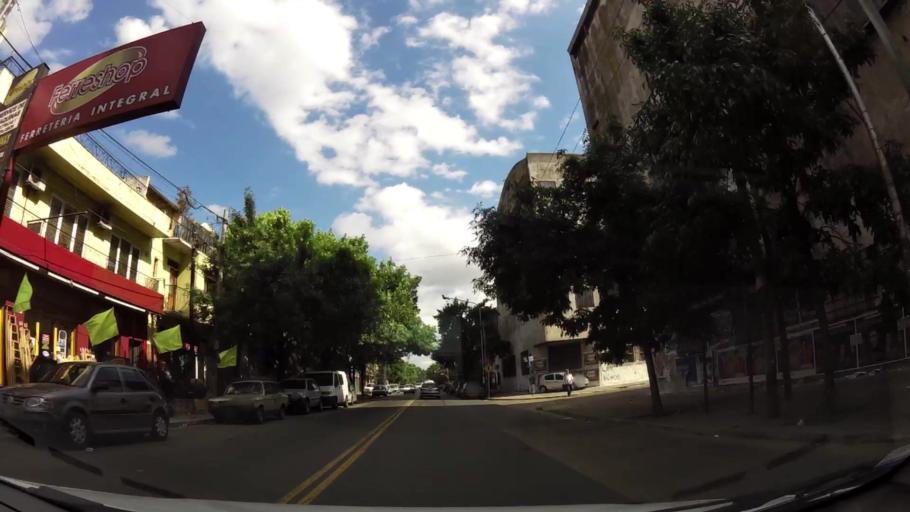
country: AR
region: Buenos Aires
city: San Justo
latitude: -34.6653
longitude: -58.5612
